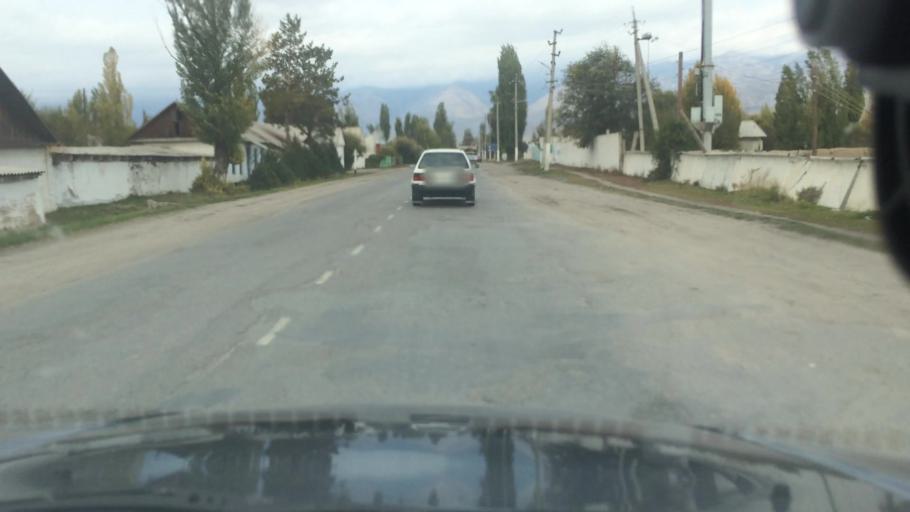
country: KG
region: Ysyk-Koel
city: Tyup
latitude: 42.7221
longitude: 78.3676
